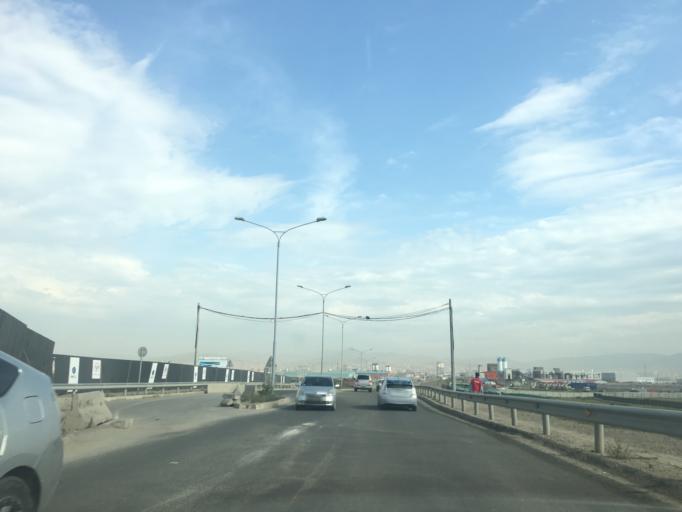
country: MN
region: Ulaanbaatar
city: Ulaanbaatar
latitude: 47.8755
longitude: 106.7843
